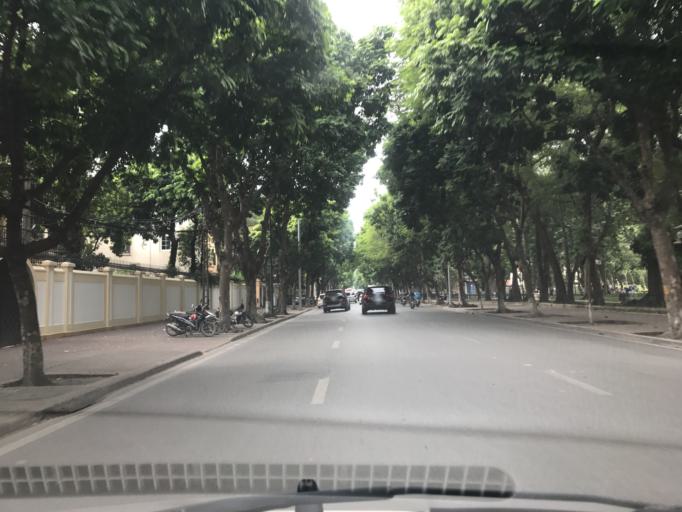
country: VN
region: Ha Noi
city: Hanoi
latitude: 21.0308
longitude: 105.8404
